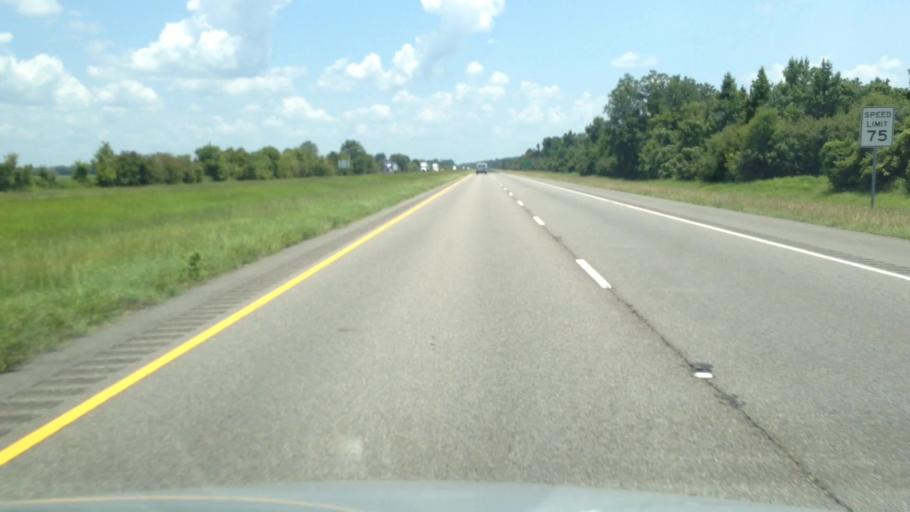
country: US
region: Louisiana
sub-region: Avoyelles Parish
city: Bunkie
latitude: 30.9431
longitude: -92.2688
